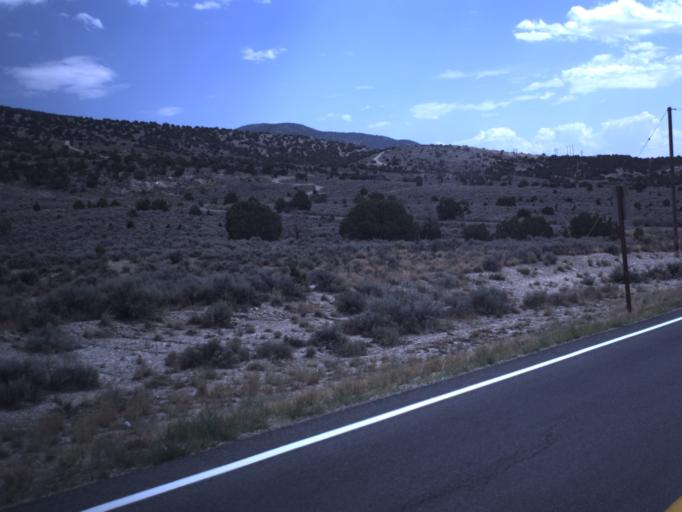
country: US
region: Utah
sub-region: Tooele County
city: Tooele
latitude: 40.3255
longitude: -112.2888
